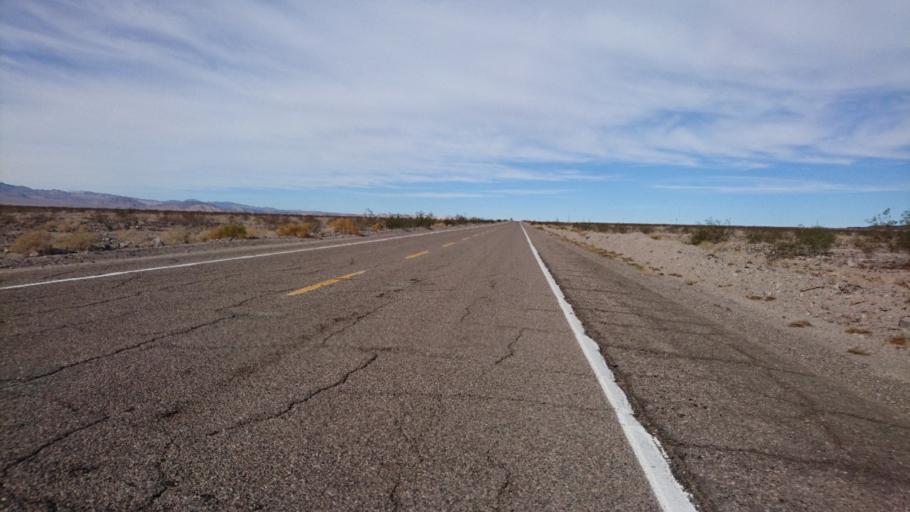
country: US
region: California
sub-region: San Bernardino County
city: Twentynine Palms
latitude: 34.5992
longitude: -115.9429
